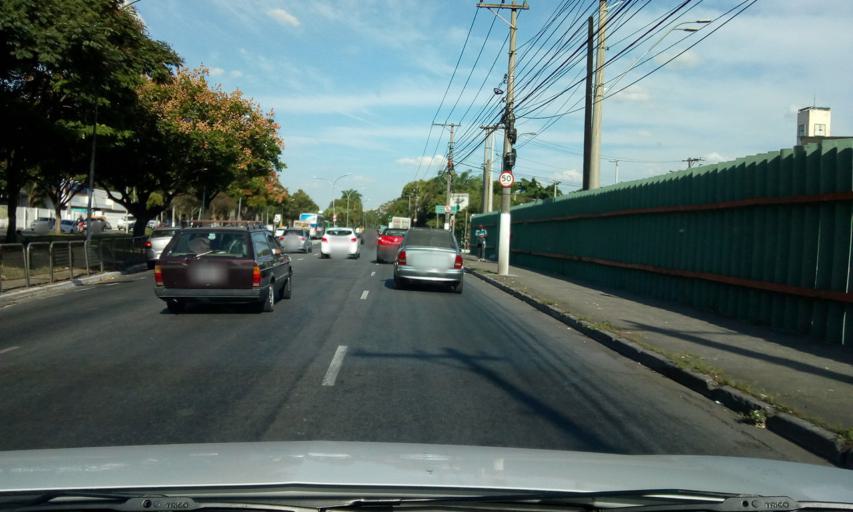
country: BR
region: Sao Paulo
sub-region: Osasco
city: Osasco
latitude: -23.5324
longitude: -46.7362
